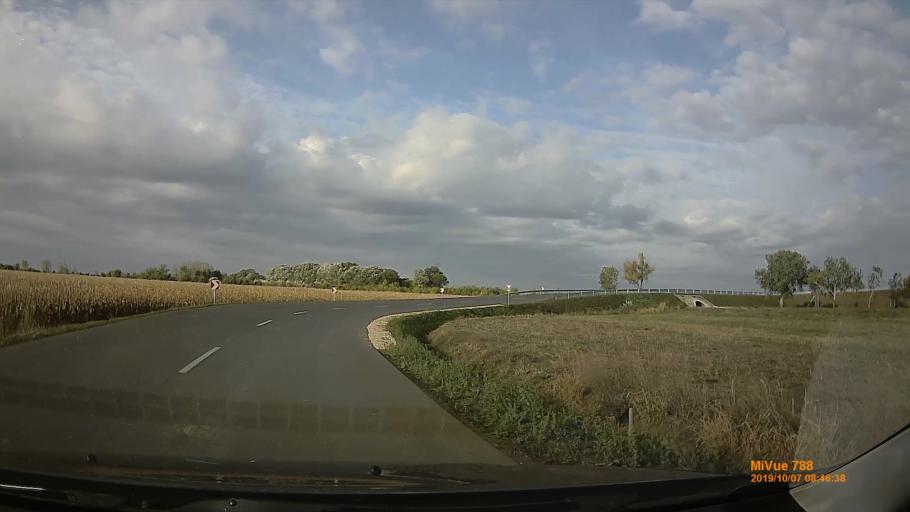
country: HU
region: Bekes
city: Szarvas
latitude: 46.8175
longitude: 20.5182
